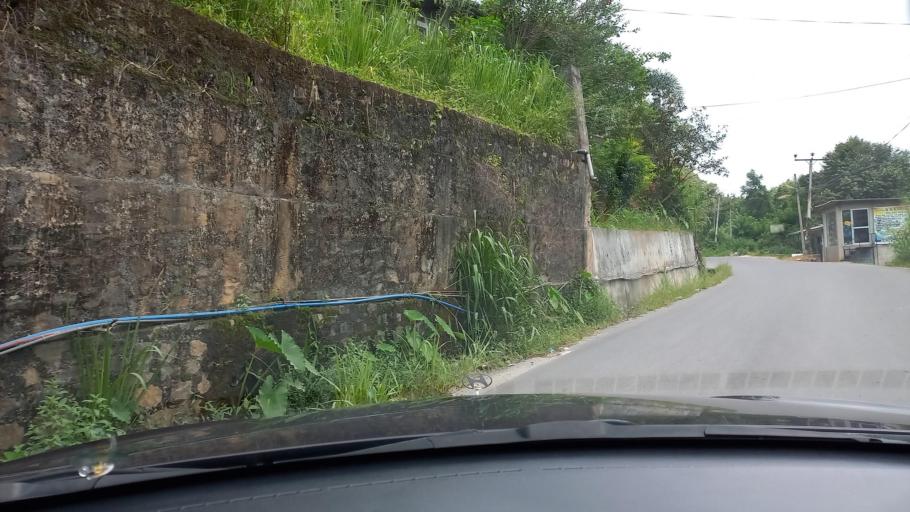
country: LK
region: Central
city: Gampola
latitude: 7.2093
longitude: 80.6261
